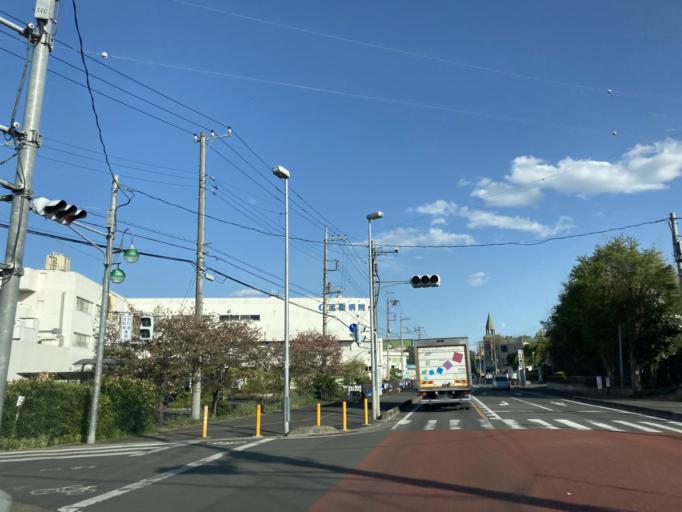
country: JP
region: Saitama
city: Sayama
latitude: 35.8824
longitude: 139.4283
